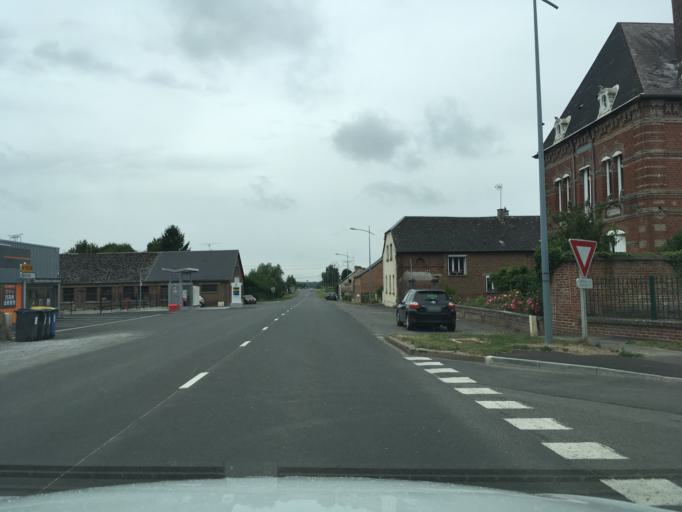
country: FR
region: Picardie
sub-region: Departement de l'Aisne
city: Buironfosse
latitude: 49.9625
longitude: 3.8305
